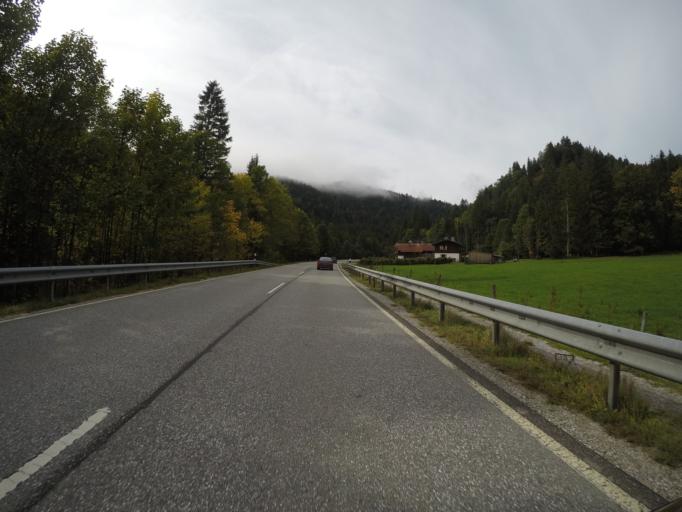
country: DE
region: Bavaria
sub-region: Upper Bavaria
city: Kreuth
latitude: 47.6127
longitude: 11.6677
